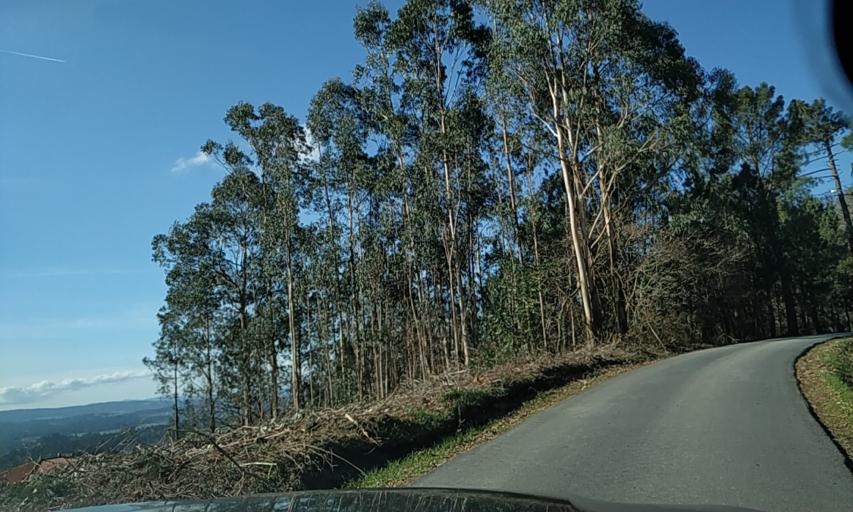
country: ES
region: Galicia
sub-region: Provincia da Coruna
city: Ribeira
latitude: 42.7039
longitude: -8.4256
